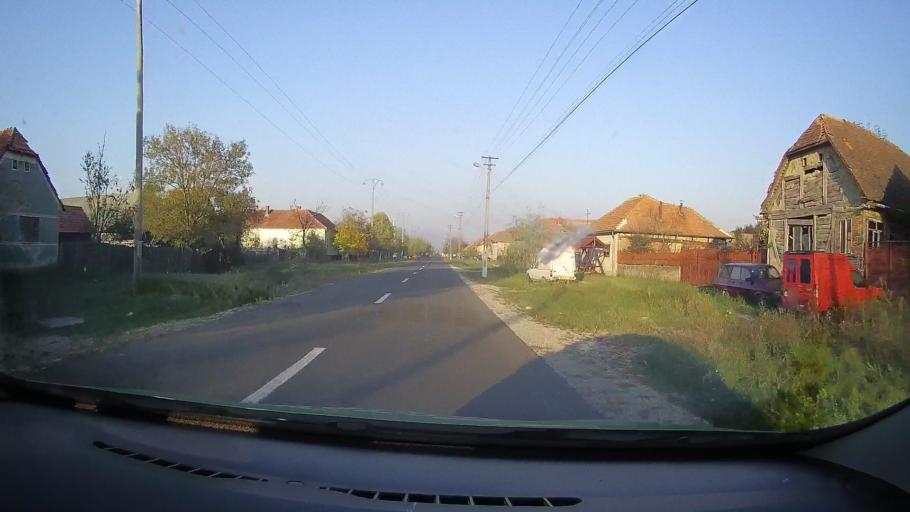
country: RO
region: Arad
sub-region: Comuna Barsa
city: Barsa
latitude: 46.3566
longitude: 22.0244
